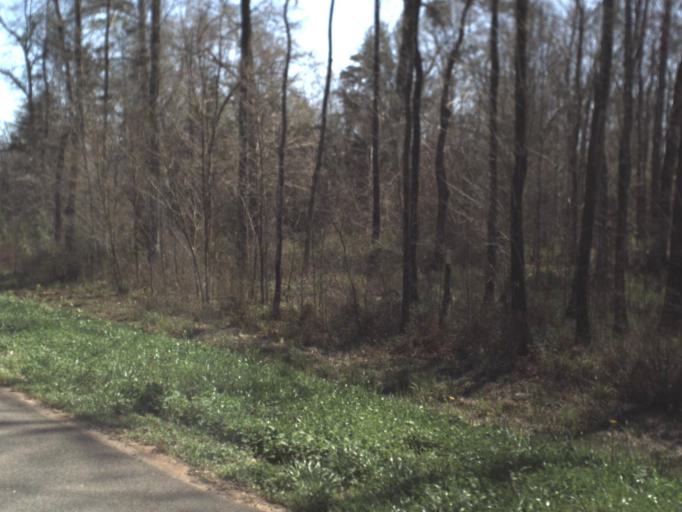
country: US
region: Florida
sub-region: Jackson County
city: Marianna
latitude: 30.8205
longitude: -85.3216
